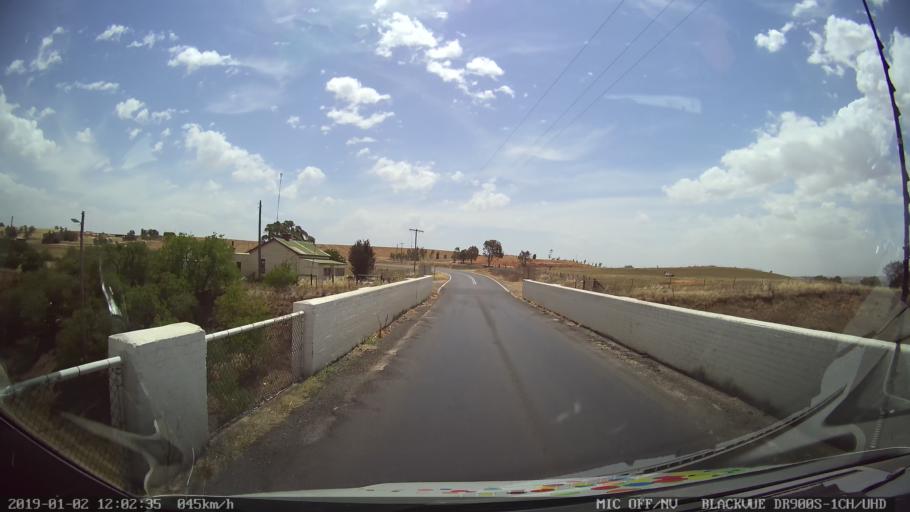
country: AU
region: New South Wales
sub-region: Young
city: Young
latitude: -34.5379
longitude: 148.3236
